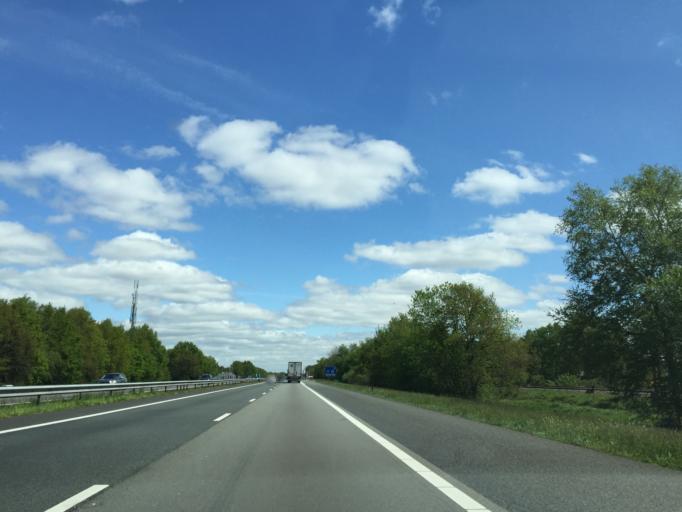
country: NL
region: Gelderland
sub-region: Gemeente Barneveld
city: Stroe
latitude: 52.1825
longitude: 5.6664
